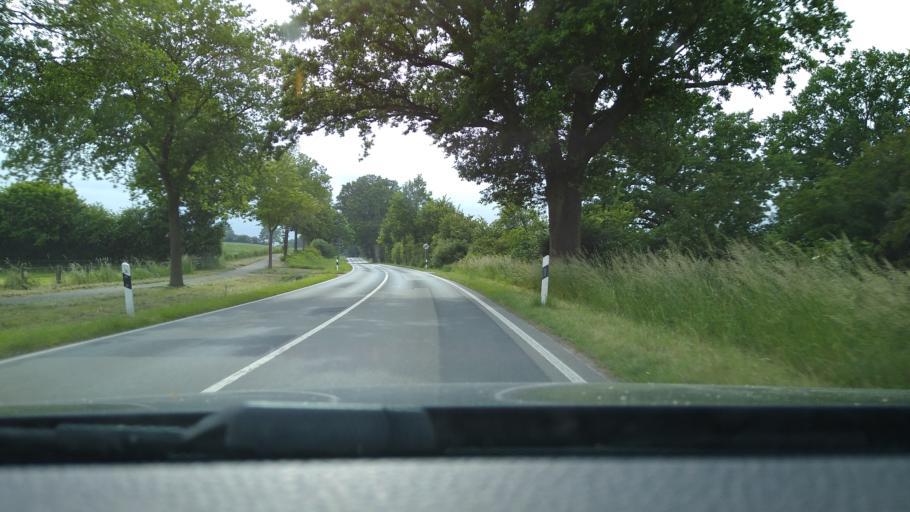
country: DE
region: Schleswig-Holstein
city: Kabelhorst
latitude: 54.2165
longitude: 10.9177
